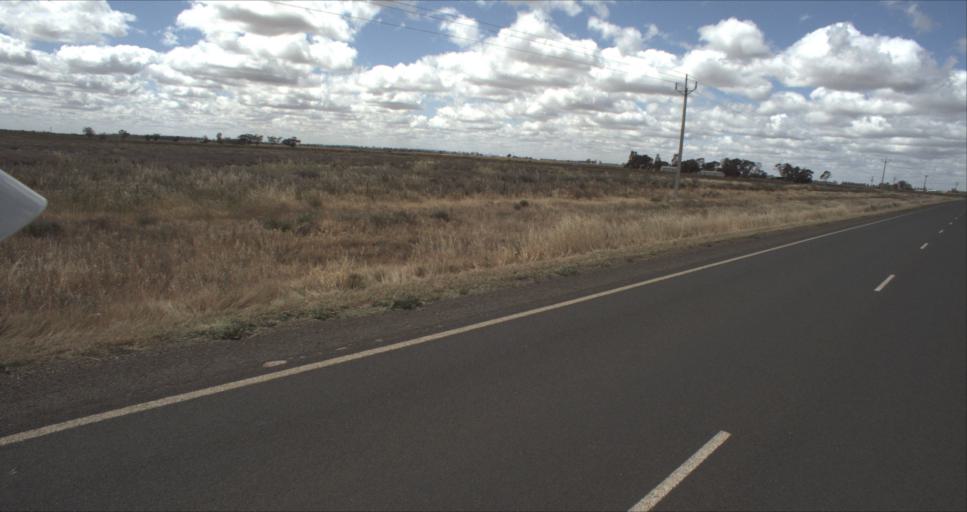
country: AU
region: New South Wales
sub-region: Murrumbidgee Shire
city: Darlington Point
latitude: -34.4915
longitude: 146.1653
